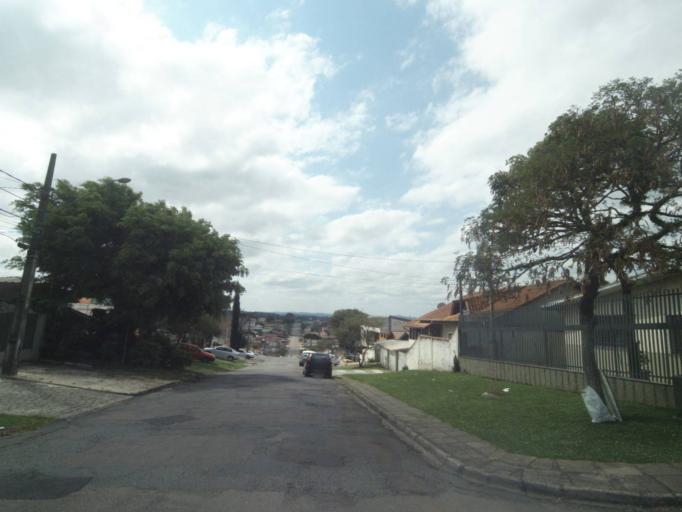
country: BR
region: Parana
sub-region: Pinhais
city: Pinhais
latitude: -25.4001
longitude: -49.2005
